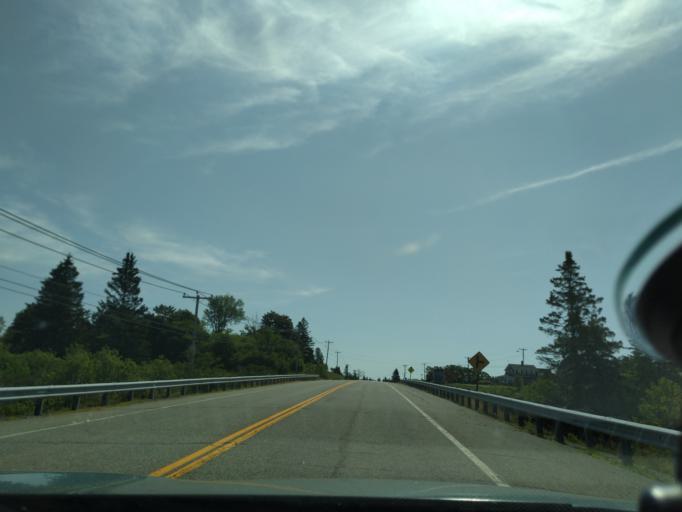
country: US
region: Maine
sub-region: Washington County
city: Addison
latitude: 44.6553
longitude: -67.7226
